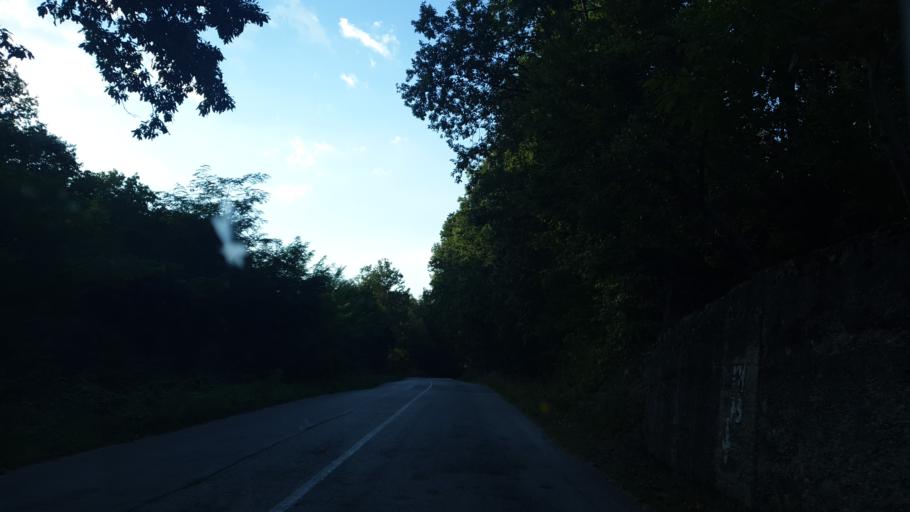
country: RS
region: Central Serbia
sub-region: Zlatiborski Okrug
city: Pozega
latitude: 43.9583
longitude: 20.0290
